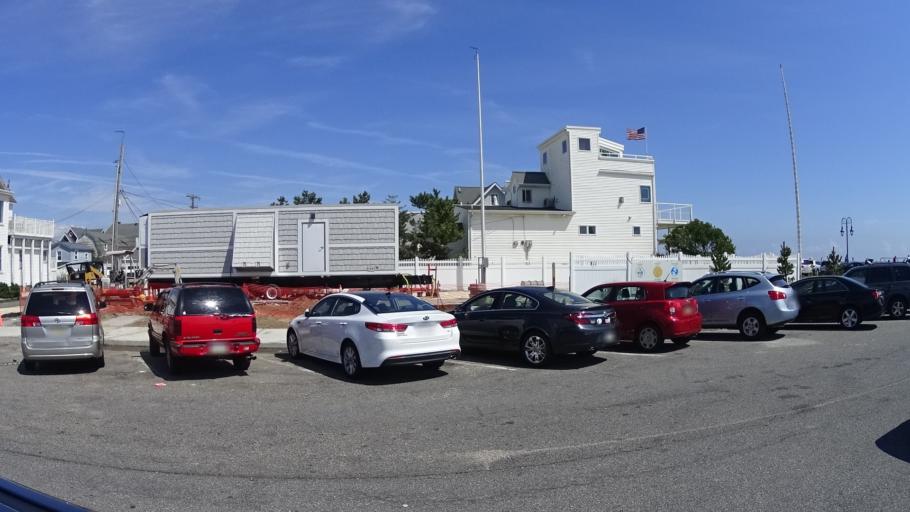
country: US
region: New Jersey
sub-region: Monmouth County
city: Belmar
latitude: 40.1790
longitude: -74.0135
